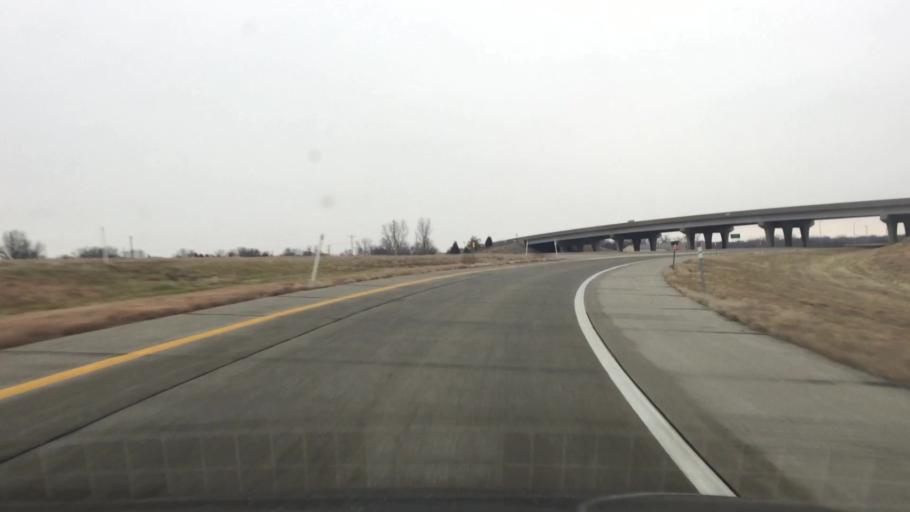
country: US
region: Kansas
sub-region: Shawnee County
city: Topeka
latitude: 39.0321
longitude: -95.6124
